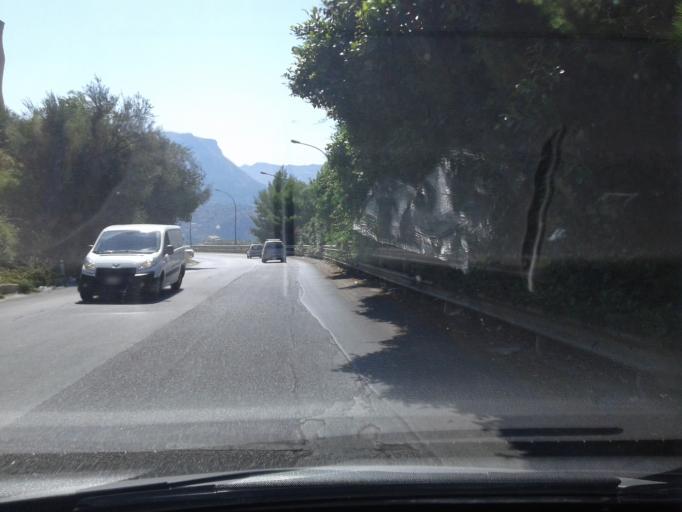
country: IT
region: Sicily
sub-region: Palermo
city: Monreale
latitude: 38.0751
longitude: 13.2825
